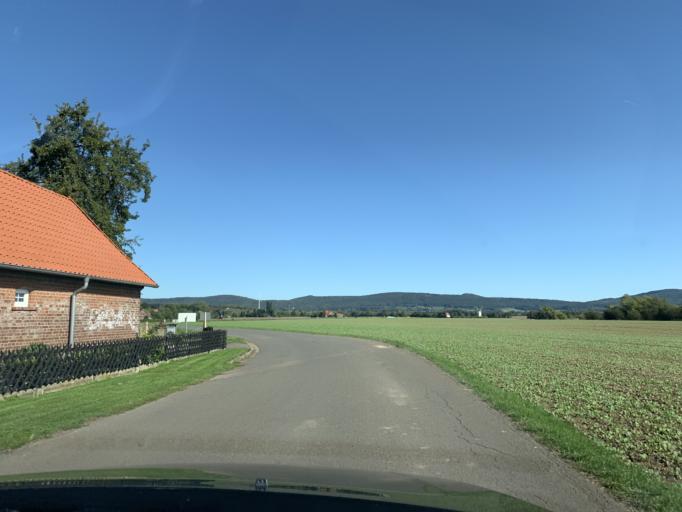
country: DE
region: North Rhine-Westphalia
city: Porta Westfalica
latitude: 52.1911
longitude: 8.9797
